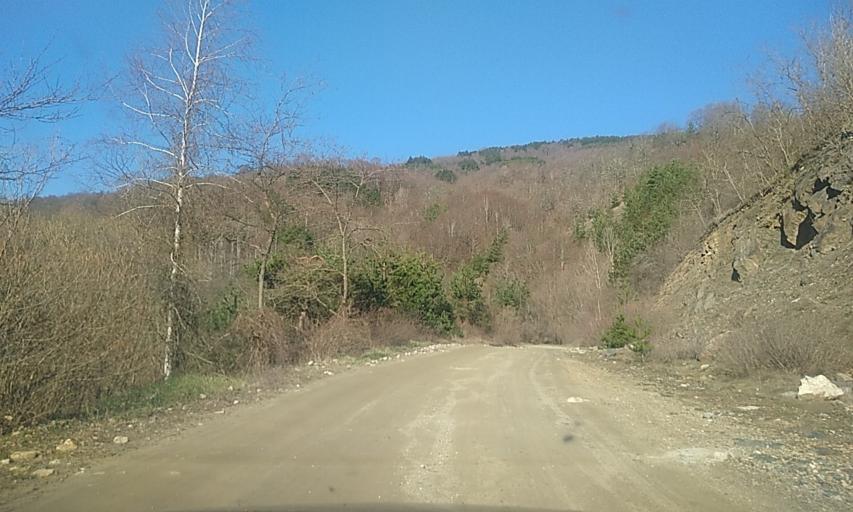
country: RS
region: Central Serbia
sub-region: Pcinjski Okrug
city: Bosilegrad
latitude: 42.3824
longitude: 22.4454
